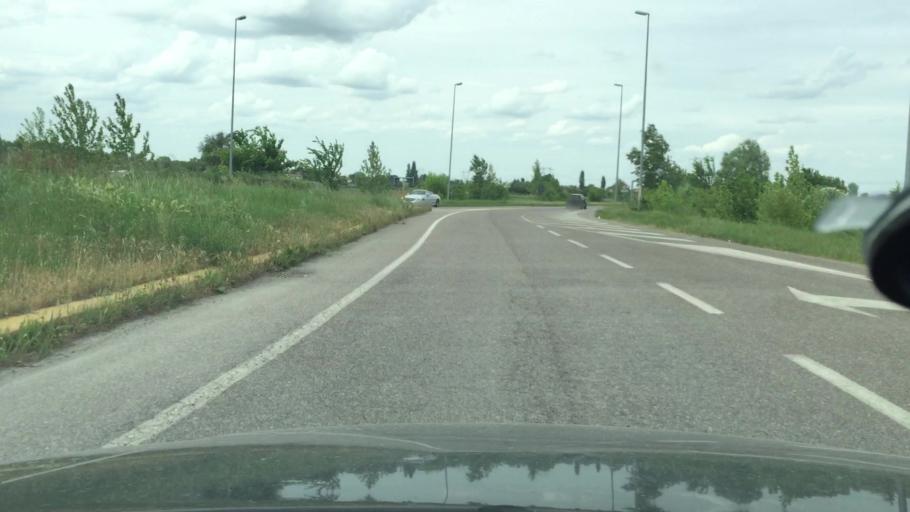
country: IT
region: Emilia-Romagna
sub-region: Provincia di Ferrara
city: Cona
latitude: 44.8055
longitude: 11.7200
